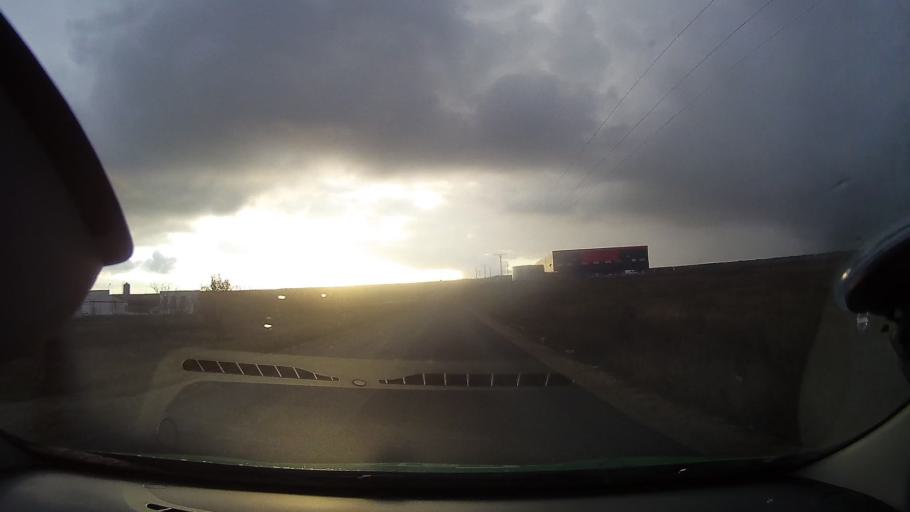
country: RO
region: Cluj
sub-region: Comuna Luna
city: Luncani
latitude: 46.4508
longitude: 23.9520
